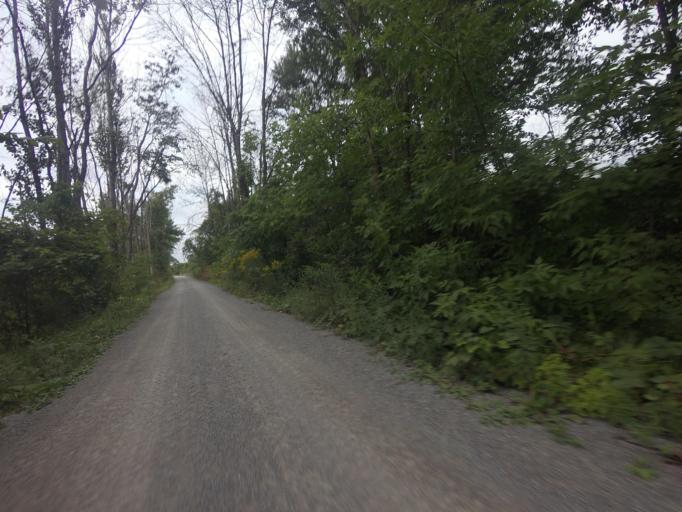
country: CA
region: Ontario
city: Omemee
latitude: 44.5282
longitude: -78.7361
